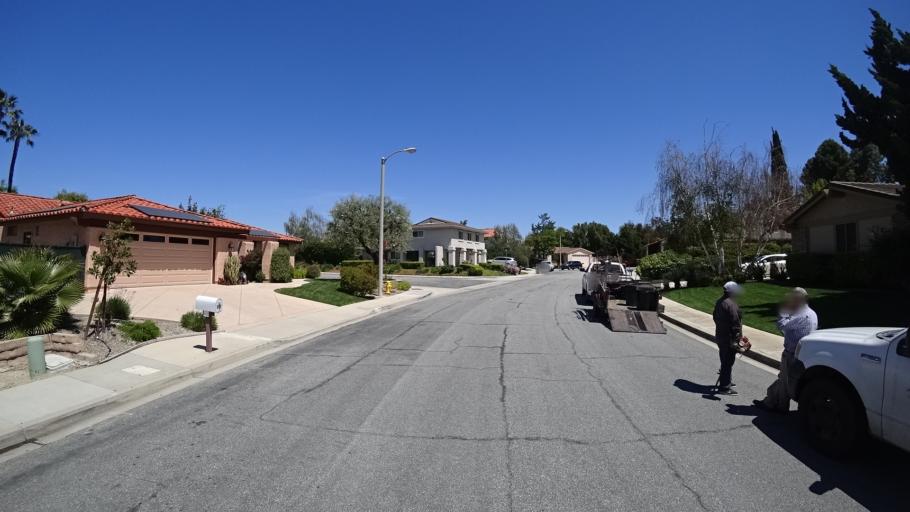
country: US
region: California
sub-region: Ventura County
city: Casa Conejo
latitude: 34.1775
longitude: -118.8915
